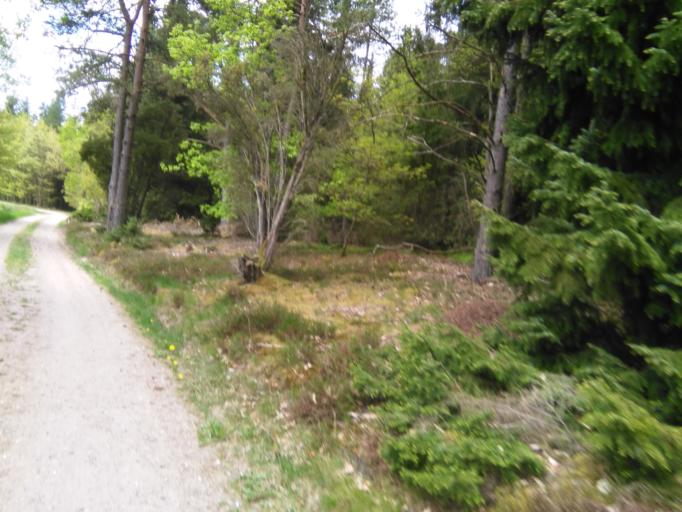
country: DK
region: Central Jutland
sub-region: Silkeborg Kommune
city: Svejbaek
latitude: 56.0645
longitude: 9.6045
